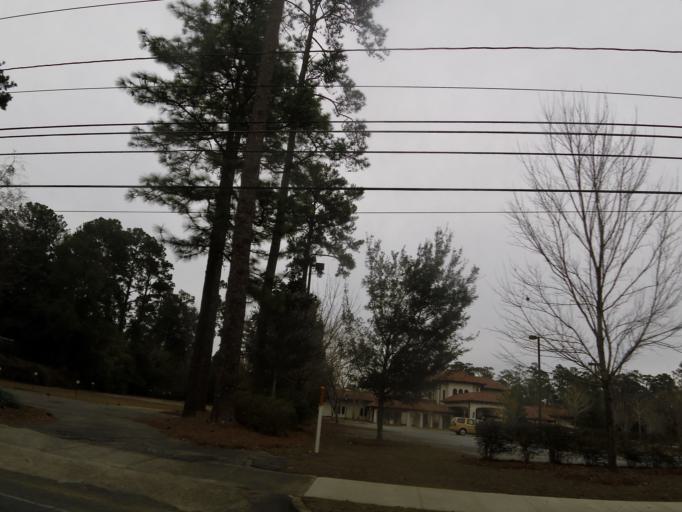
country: US
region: Georgia
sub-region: Thomas County
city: Thomasville
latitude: 30.8278
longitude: -83.9713
